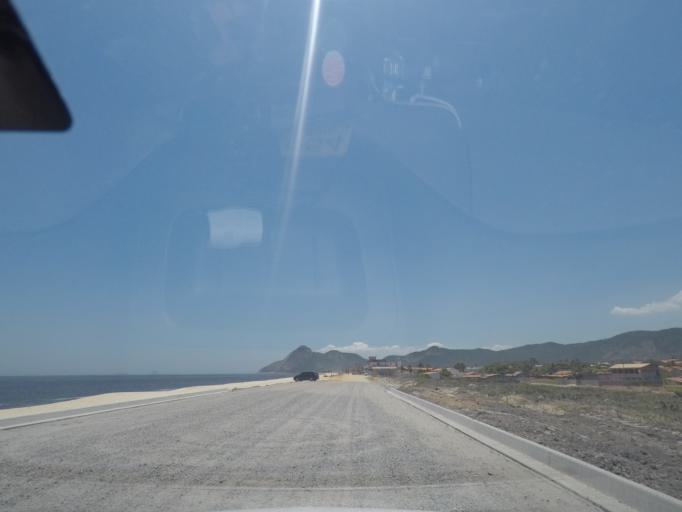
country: BR
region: Rio de Janeiro
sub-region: Marica
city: Marica
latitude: -22.9696
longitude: -42.9656
